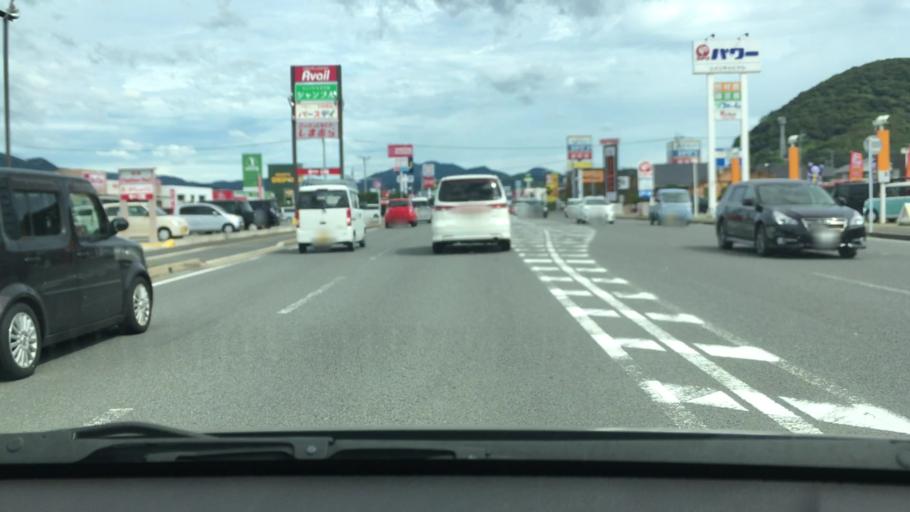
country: JP
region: Nagasaki
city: Togitsu
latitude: 32.8522
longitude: 129.8255
